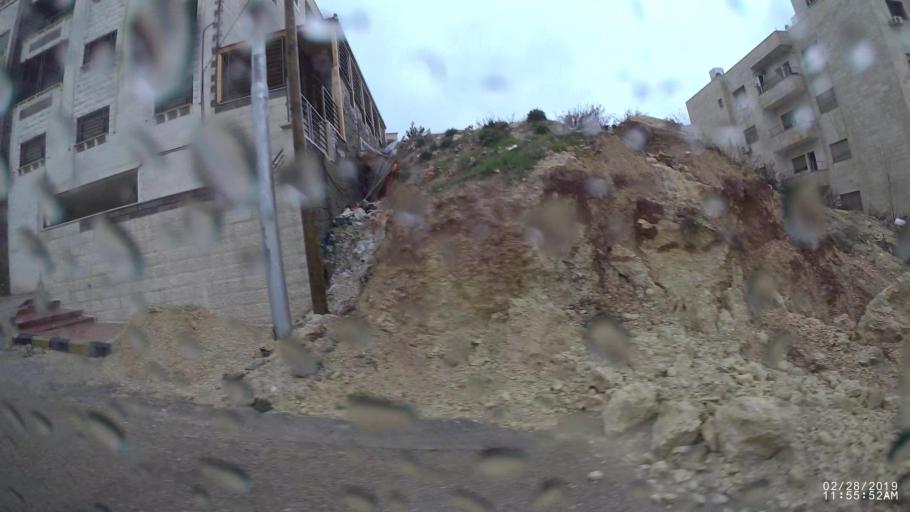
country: JO
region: Amman
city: Al Jubayhah
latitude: 32.0195
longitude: 35.8937
